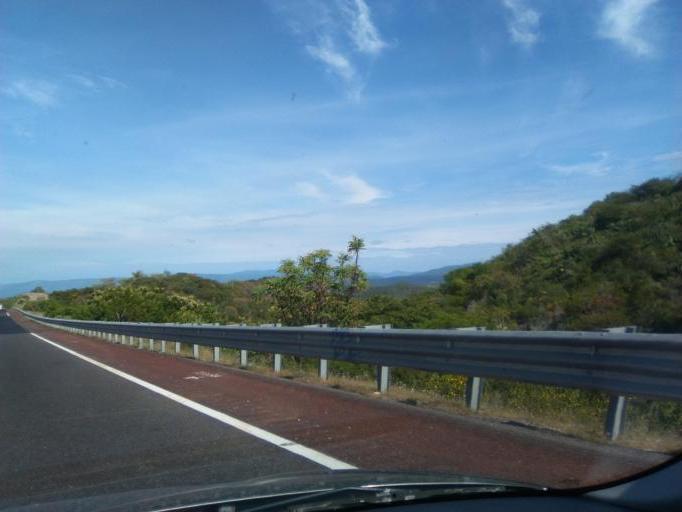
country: MX
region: Guerrero
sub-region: Huitzuco de los Figueroa
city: San Francisco Ozomatlan
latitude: 18.0683
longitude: -99.2411
